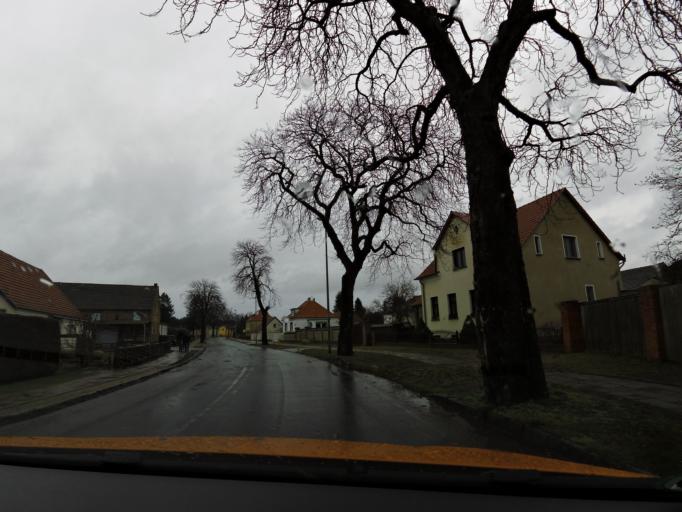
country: DE
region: Brandenburg
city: Am Mellensee
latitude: 52.1857
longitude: 13.4195
